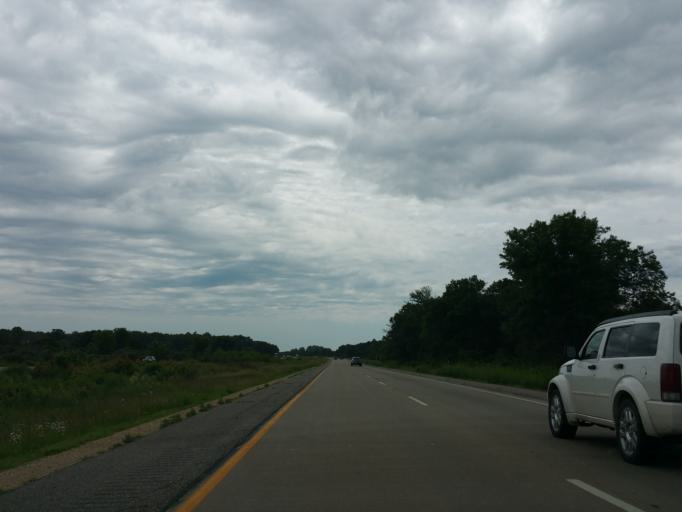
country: US
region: Wisconsin
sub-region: Juneau County
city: Mauston
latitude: 43.8288
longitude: -90.0875
